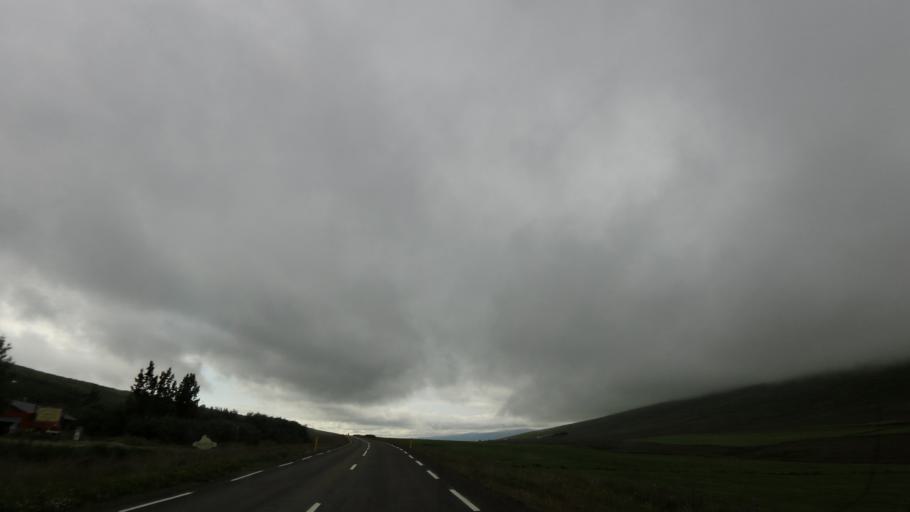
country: IS
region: Northeast
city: Laugar
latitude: 65.7812
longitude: -17.5808
